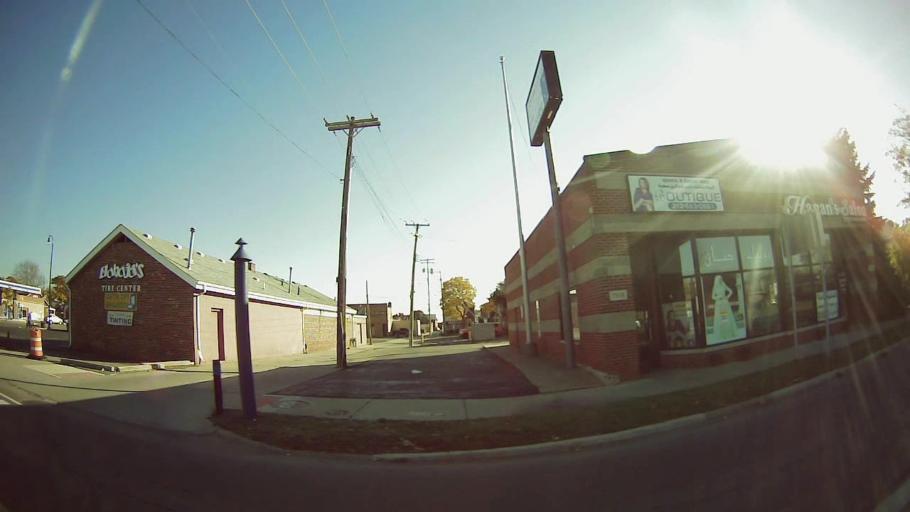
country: US
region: Michigan
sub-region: Wayne County
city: Dearborn
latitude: 42.3432
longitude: -83.1962
